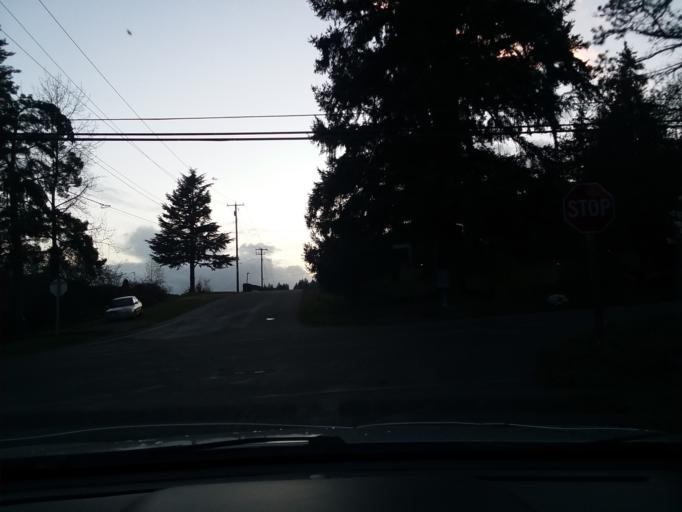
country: US
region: Washington
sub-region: King County
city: Kenmore
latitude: 47.7627
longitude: -122.2569
